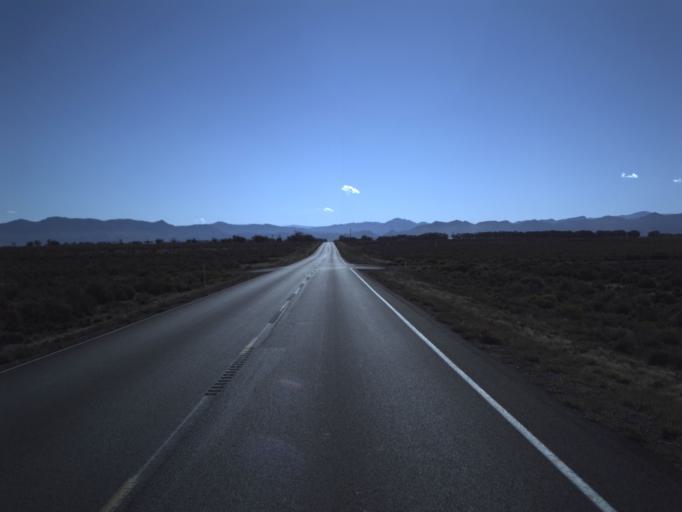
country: US
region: Utah
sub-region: Washington County
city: Enterprise
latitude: 37.7296
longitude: -113.7123
